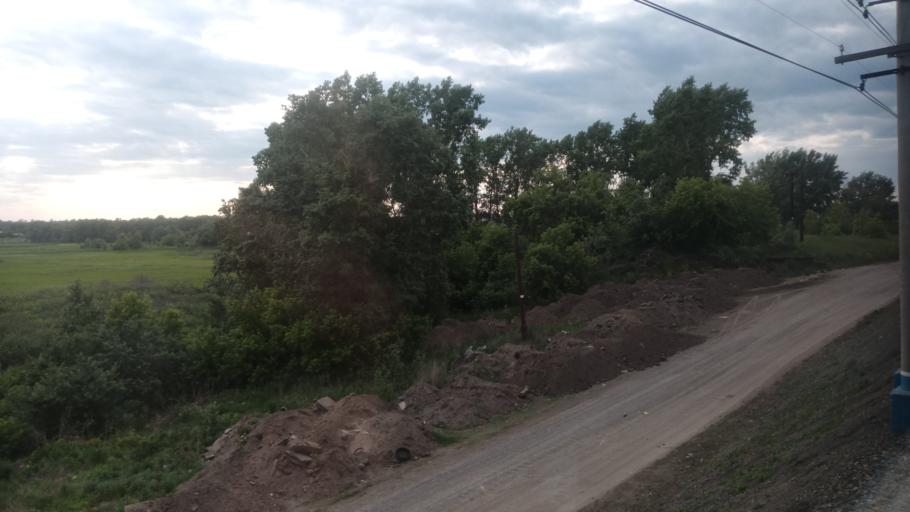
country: RU
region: Altai Krai
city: Beloyarsk
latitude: 53.4180
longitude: 83.9149
